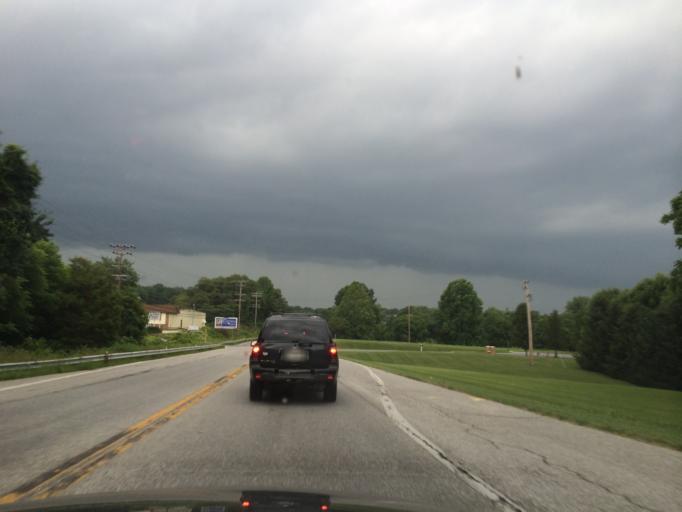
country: US
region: Maryland
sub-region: Carroll County
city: Eldersburg
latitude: 39.4115
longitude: -76.9746
